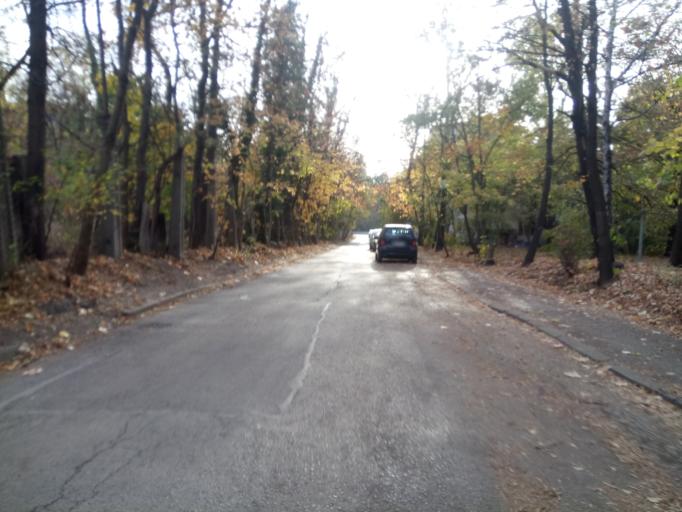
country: BG
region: Sofia-Capital
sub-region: Stolichna Obshtina
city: Sofia
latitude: 42.6825
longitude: 23.3527
